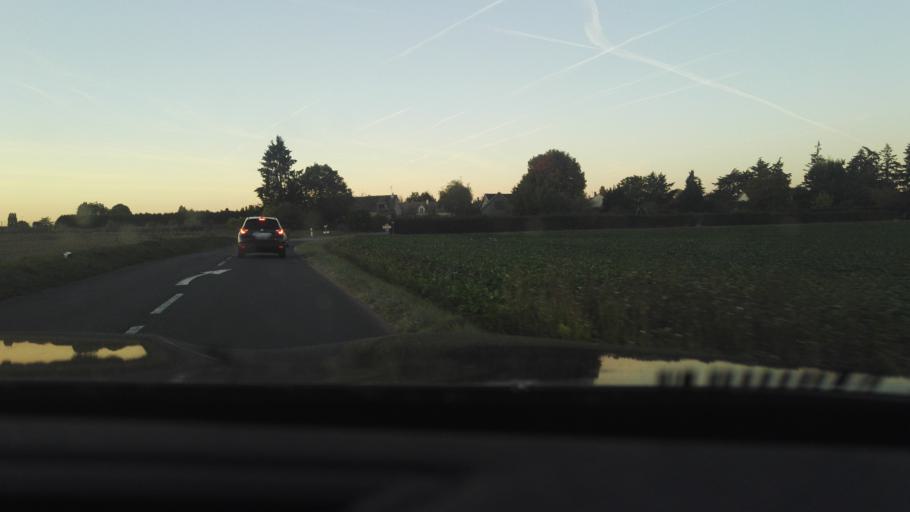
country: FR
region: Ile-de-France
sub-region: Departement des Yvelines
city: Longnes
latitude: 48.8558
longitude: 1.5898
